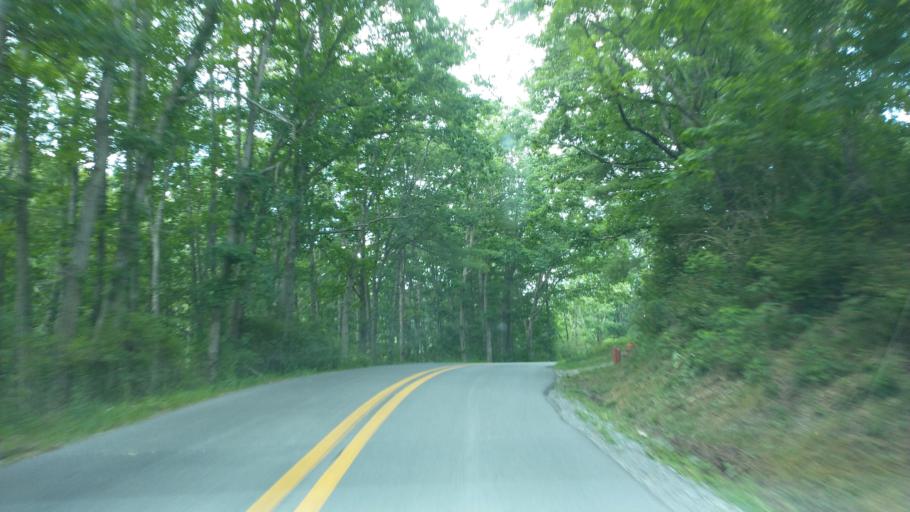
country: US
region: West Virginia
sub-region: Mercer County
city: Athens
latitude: 37.4365
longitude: -81.0620
